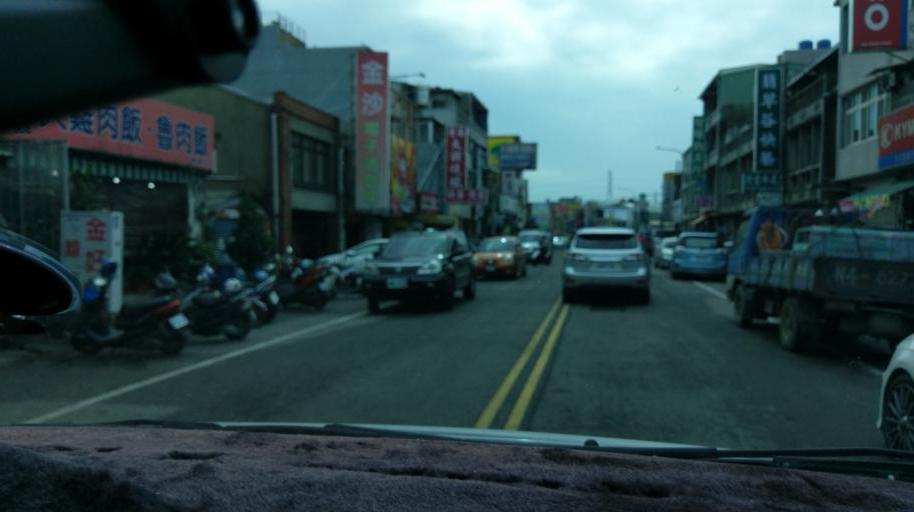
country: TW
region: Taiwan
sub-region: Miaoli
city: Miaoli
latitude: 24.4907
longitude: 120.6790
